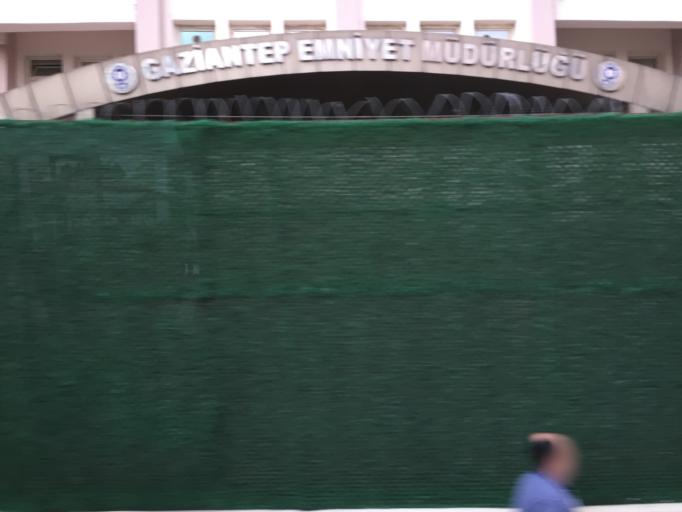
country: TR
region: Gaziantep
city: Gaziantep
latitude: 37.0675
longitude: 37.3742
